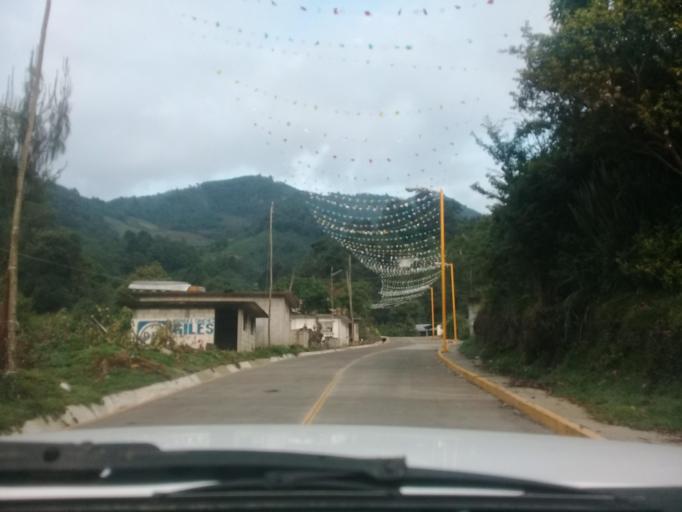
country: MX
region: Veracruz
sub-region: Mariano Escobedo
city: San Isidro el Berro
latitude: 18.9552
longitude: -97.1956
